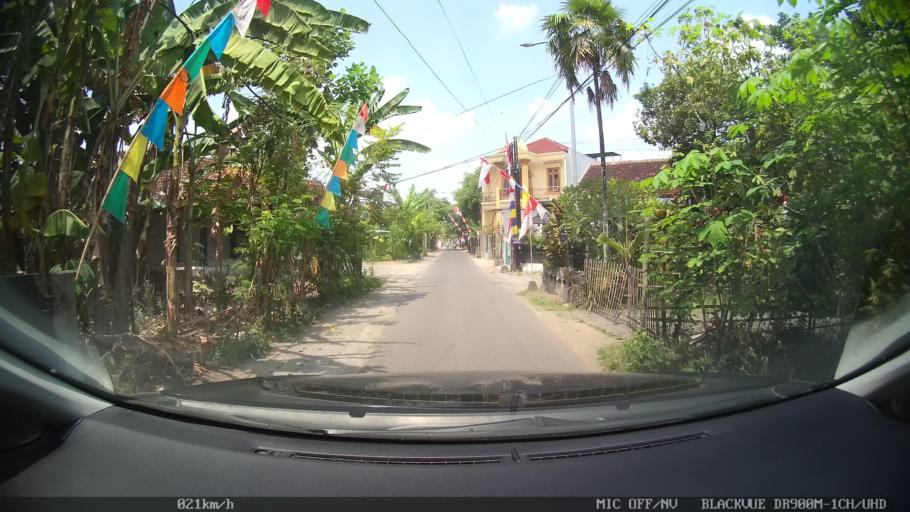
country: ID
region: Daerah Istimewa Yogyakarta
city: Yogyakarta
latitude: -7.8235
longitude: 110.4061
